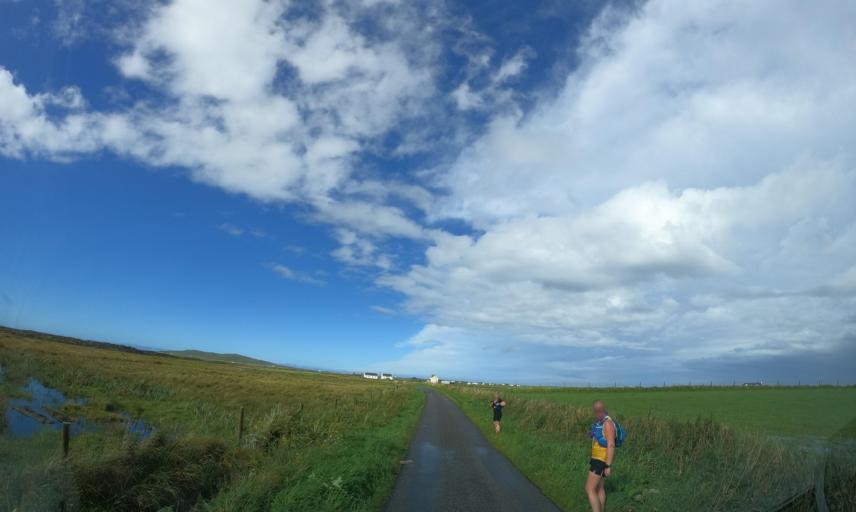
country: GB
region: Scotland
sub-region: Eilean Siar
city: Barra
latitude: 56.5210
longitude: -6.8973
